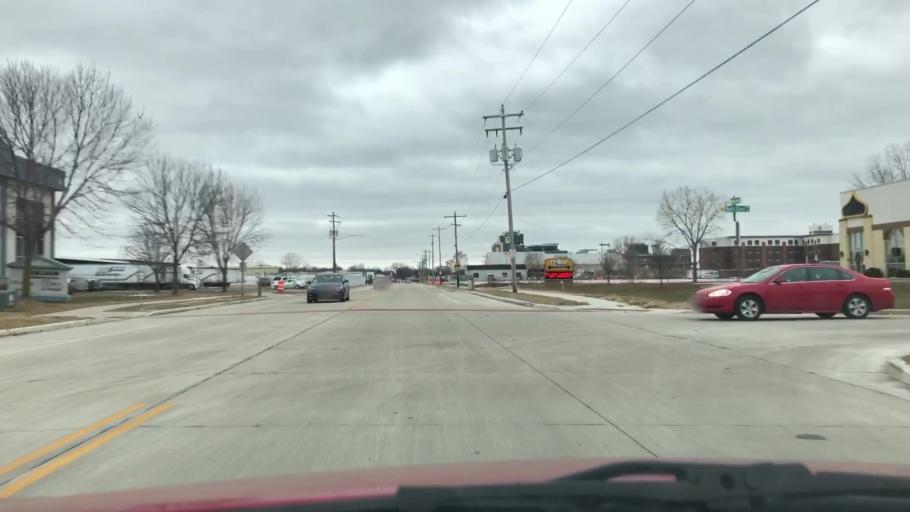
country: US
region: Wisconsin
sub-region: Brown County
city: Ashwaubenon
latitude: 44.4938
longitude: -88.0483
